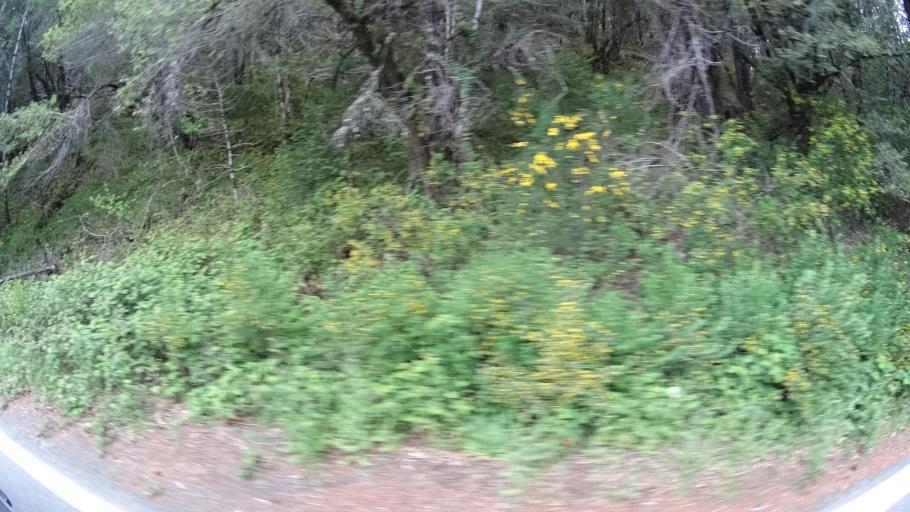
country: US
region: California
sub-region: Humboldt County
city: Redway
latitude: 40.1132
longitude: -123.8904
